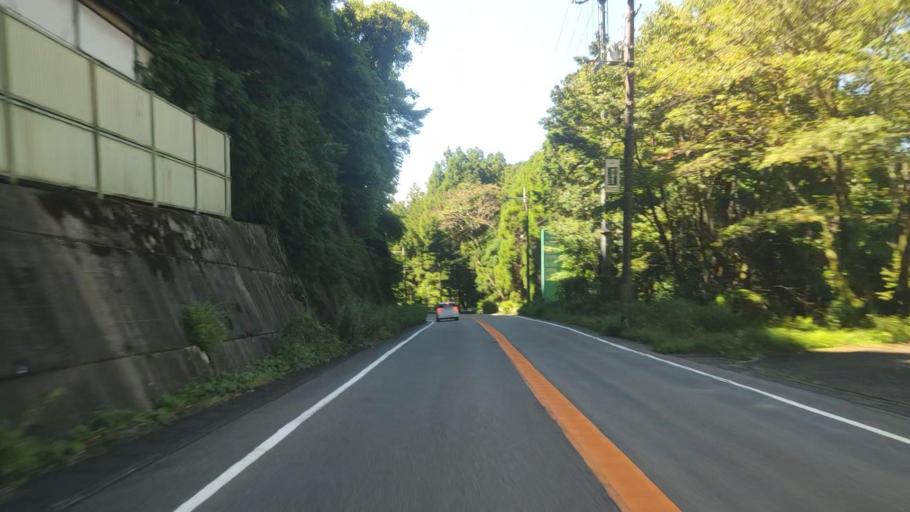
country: JP
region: Nara
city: Yoshino-cho
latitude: 34.3744
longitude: 135.9134
